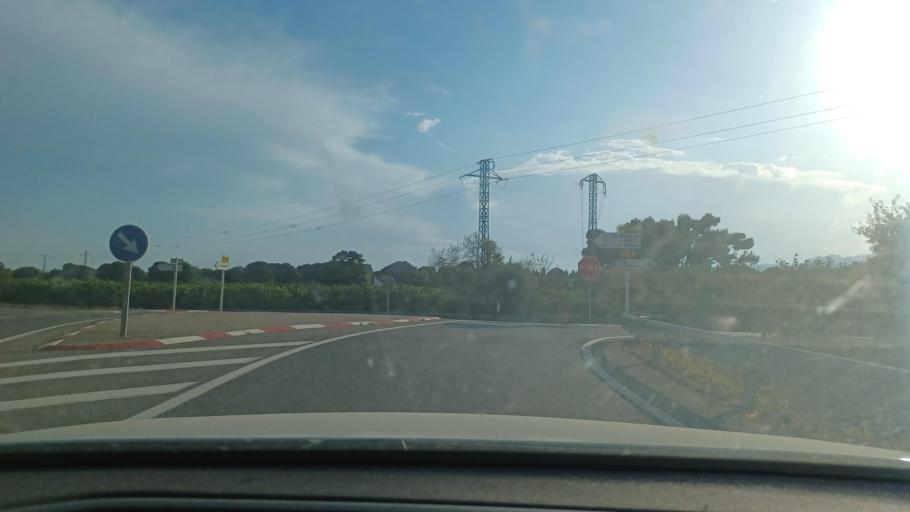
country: ES
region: Catalonia
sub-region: Provincia de Tarragona
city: Santa Barbara
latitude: 40.7108
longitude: 0.4857
